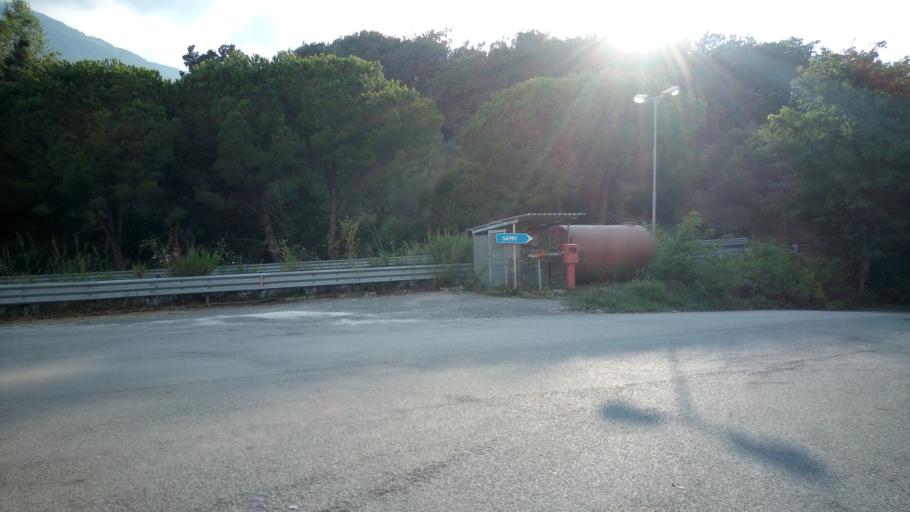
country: IT
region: Campania
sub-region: Provincia di Salerno
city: Roccagloriosa
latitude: 40.0903
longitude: 15.4545
